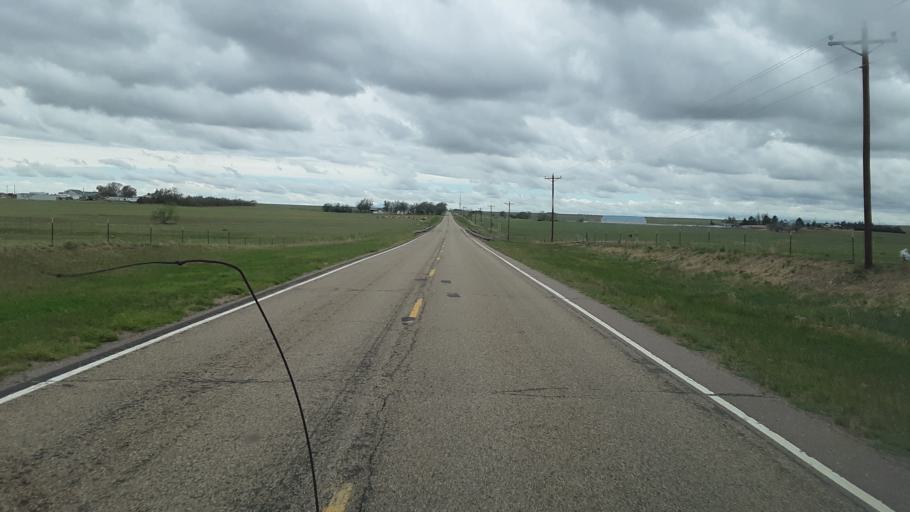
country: US
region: Colorado
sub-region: El Paso County
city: Ellicott
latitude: 38.8398
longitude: -103.9891
